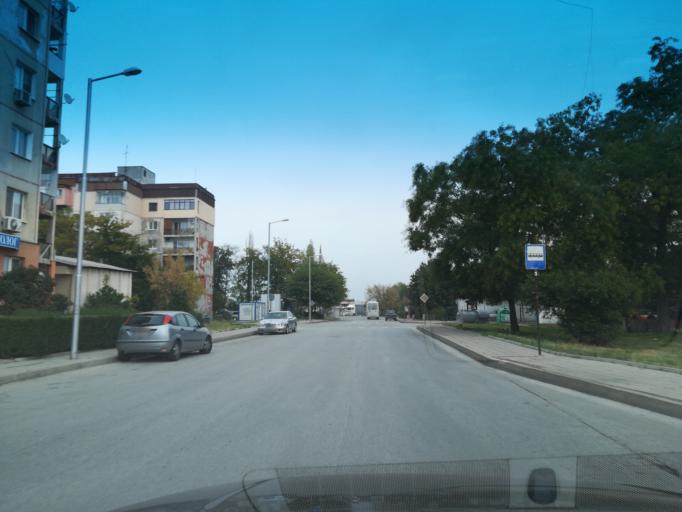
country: BG
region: Plovdiv
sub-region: Obshtina Plovdiv
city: Plovdiv
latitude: 42.1449
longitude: 24.7995
